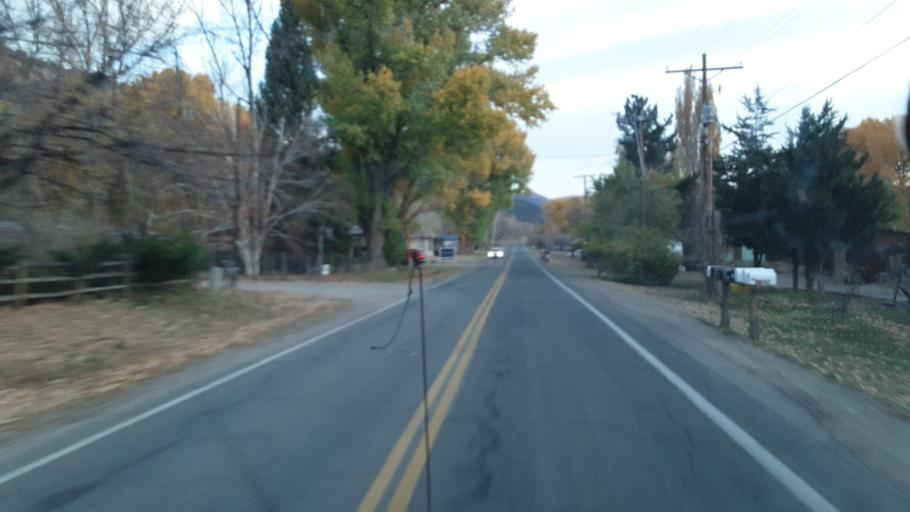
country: US
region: Colorado
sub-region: La Plata County
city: Durango
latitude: 37.3338
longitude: -107.8549
